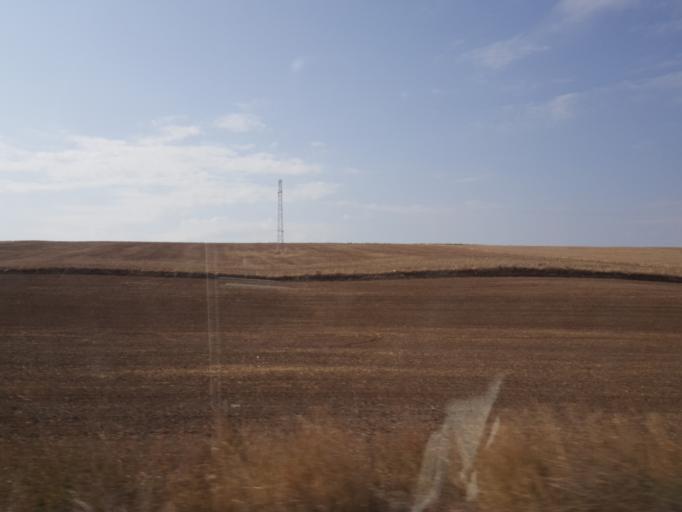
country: TR
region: Corum
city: Cemilbey
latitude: 40.1752
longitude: 35.0383
